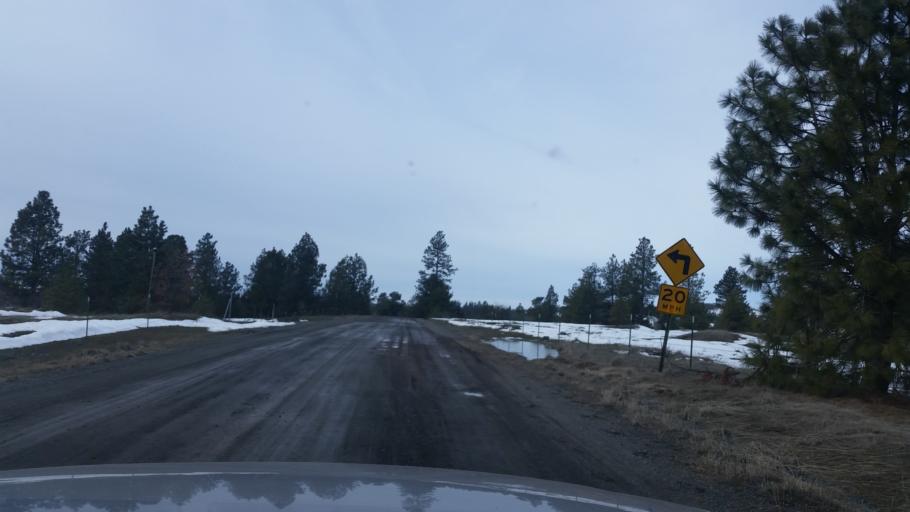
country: US
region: Washington
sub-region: Spokane County
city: Fairchild Air Force Base
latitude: 47.5801
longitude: -117.6417
